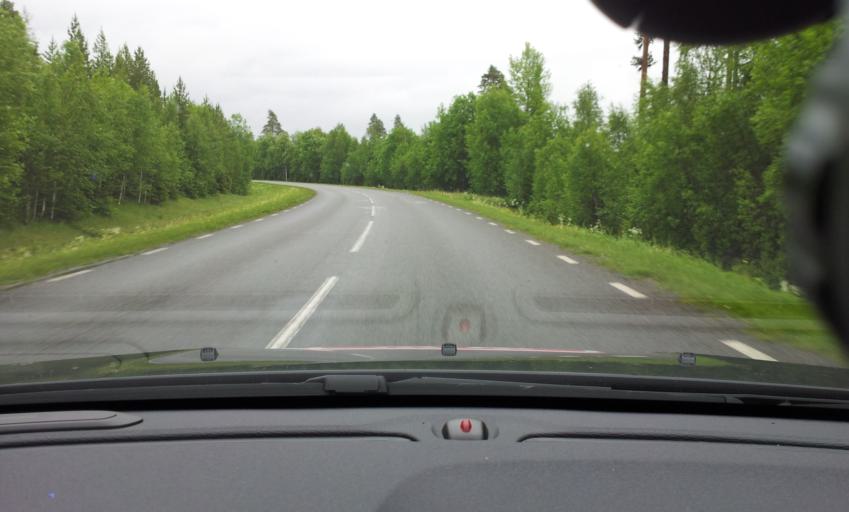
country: SE
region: Jaemtland
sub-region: Stroemsunds Kommun
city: Stroemsund
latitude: 63.5982
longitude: 15.3117
